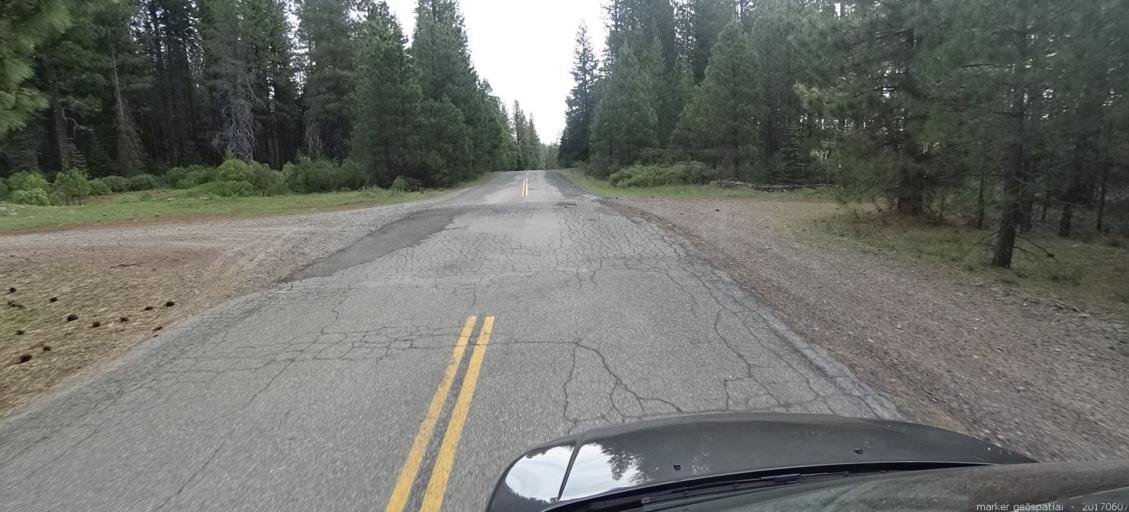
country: US
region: California
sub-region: Shasta County
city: Burney
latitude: 41.1906
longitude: -121.7006
